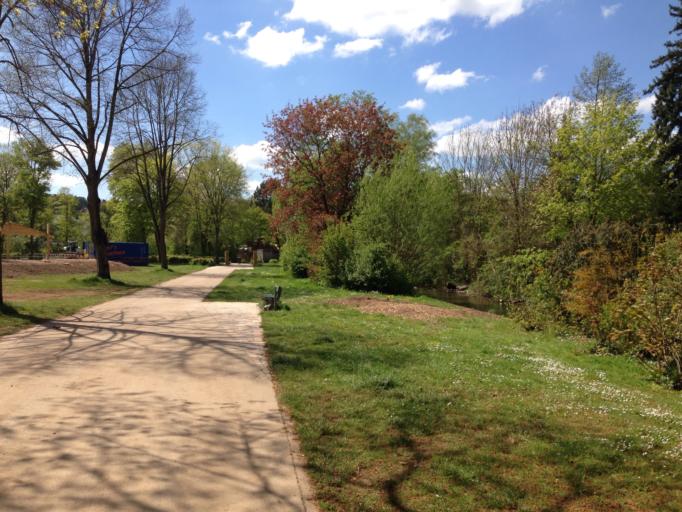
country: DE
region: Hesse
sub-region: Regierungsbezirk Giessen
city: Lich
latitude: 50.5178
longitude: 8.8218
